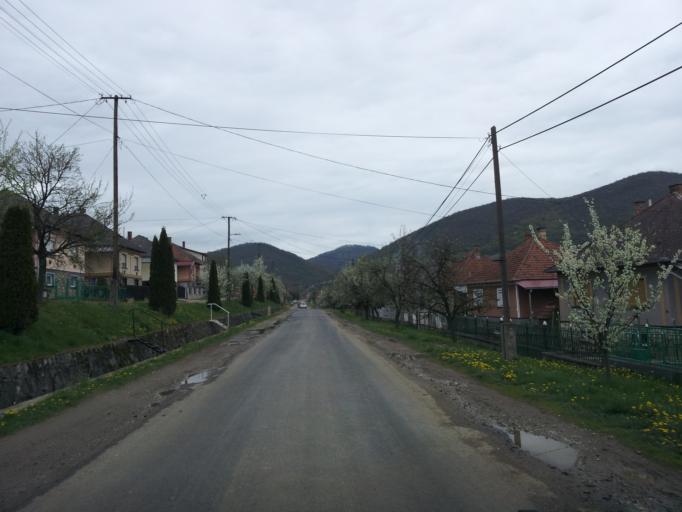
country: HU
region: Borsod-Abauj-Zemplen
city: Szendro
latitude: 48.5155
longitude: 20.6798
